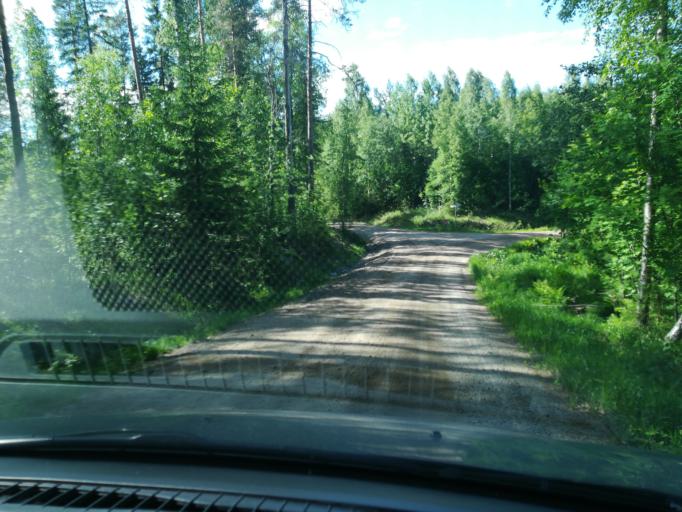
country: FI
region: Southern Savonia
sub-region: Mikkeli
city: Puumala
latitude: 61.6516
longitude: 28.1776
